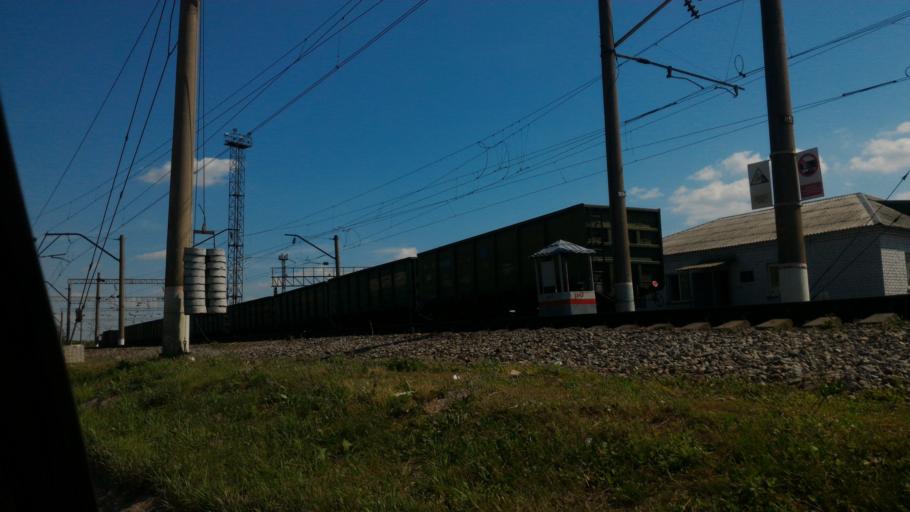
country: RU
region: Rjazan
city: Rybnoye
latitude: 54.7297
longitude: 39.5089
